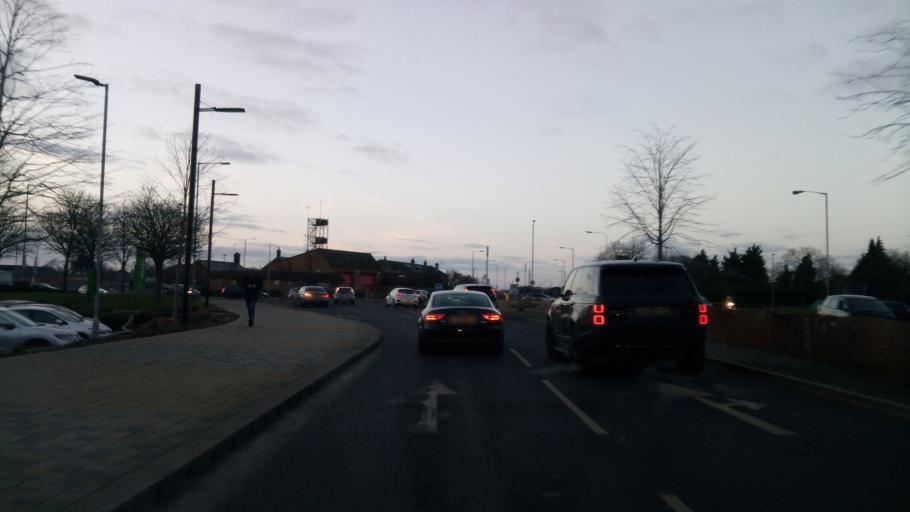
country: GB
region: England
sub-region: Peterborough
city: Peterborough
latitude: 52.5761
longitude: -0.2490
